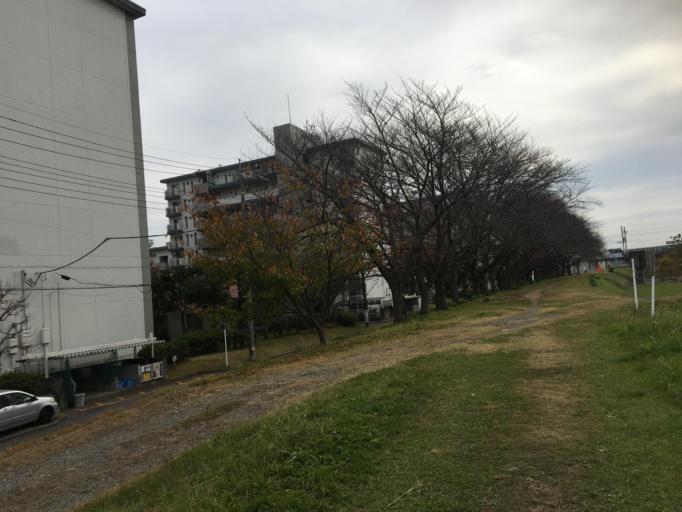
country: JP
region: Saitama
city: Yoshikawa
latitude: 35.8790
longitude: 139.8408
